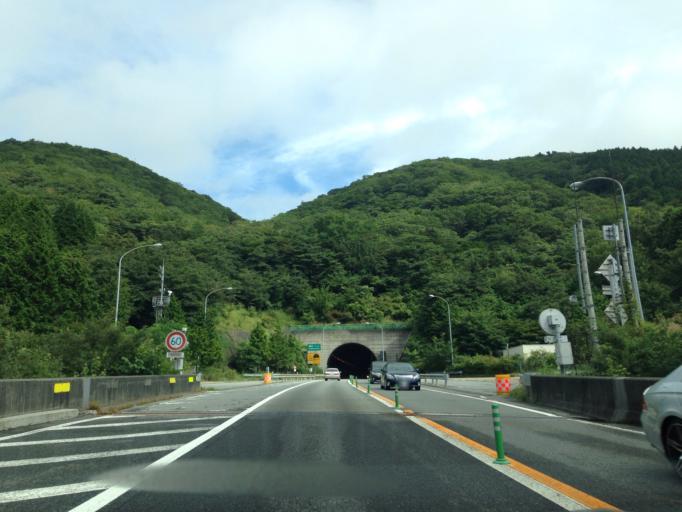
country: JP
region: Shizuoka
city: Gotemba
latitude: 35.3790
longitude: 138.8450
